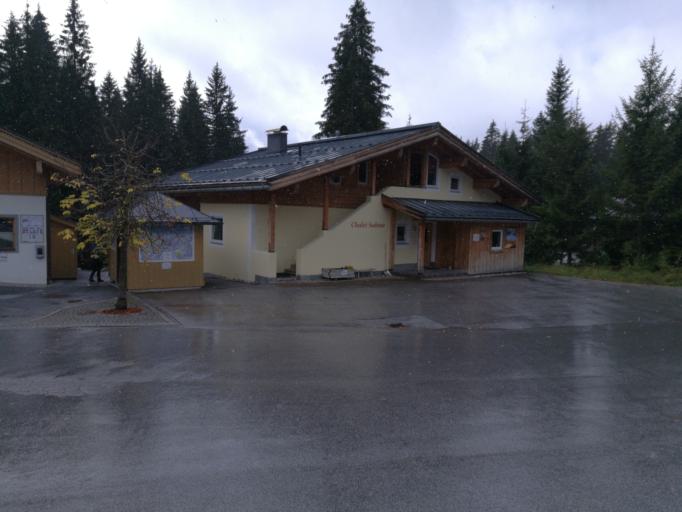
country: AT
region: Salzburg
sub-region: Politischer Bezirk Zell am See
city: Krimml
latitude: 47.2470
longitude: 12.1178
